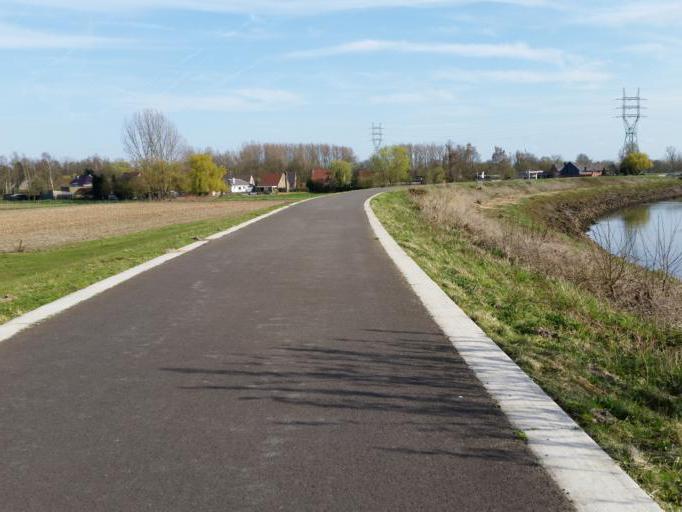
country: BE
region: Flanders
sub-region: Provincie Antwerpen
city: Rumst
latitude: 51.0381
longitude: 4.4210
